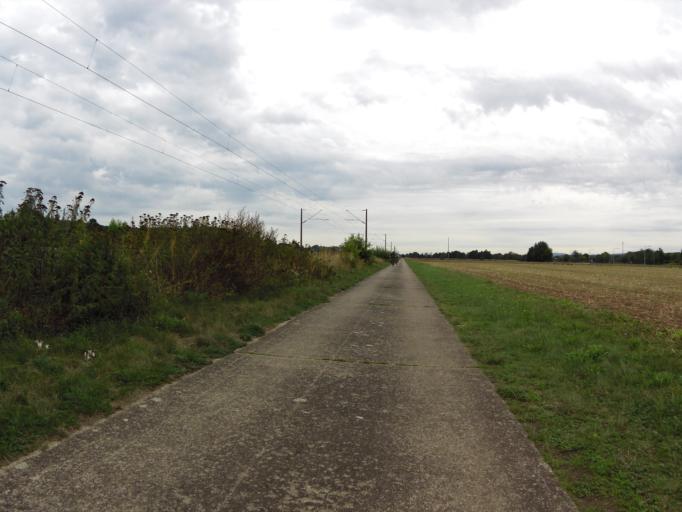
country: DE
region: Bavaria
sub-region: Regierungsbezirk Unterfranken
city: Gadheim
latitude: 50.0177
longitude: 10.3827
